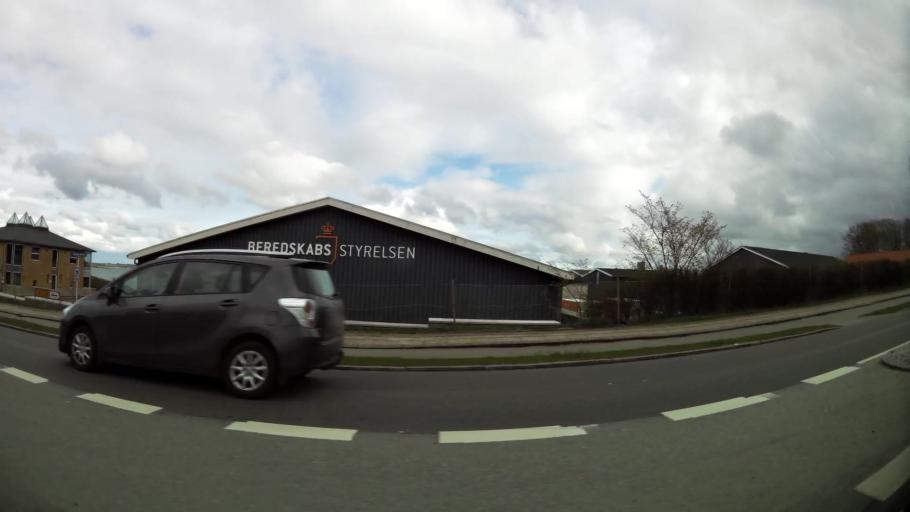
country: DK
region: North Denmark
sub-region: Thisted Kommune
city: Thisted
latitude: 56.9487
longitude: 8.6628
